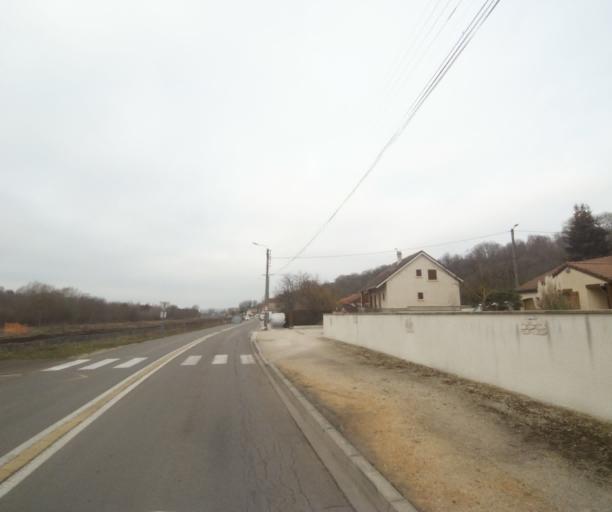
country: FR
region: Lorraine
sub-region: Departement de la Meuse
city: Ancerville
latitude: 48.6288
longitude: 4.9920
